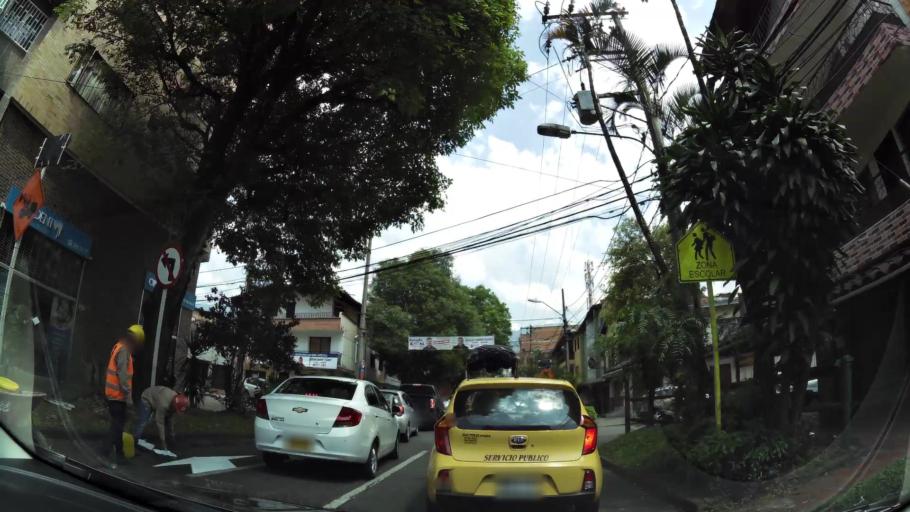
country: CO
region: Antioquia
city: Envigado
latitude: 6.1693
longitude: -75.5903
